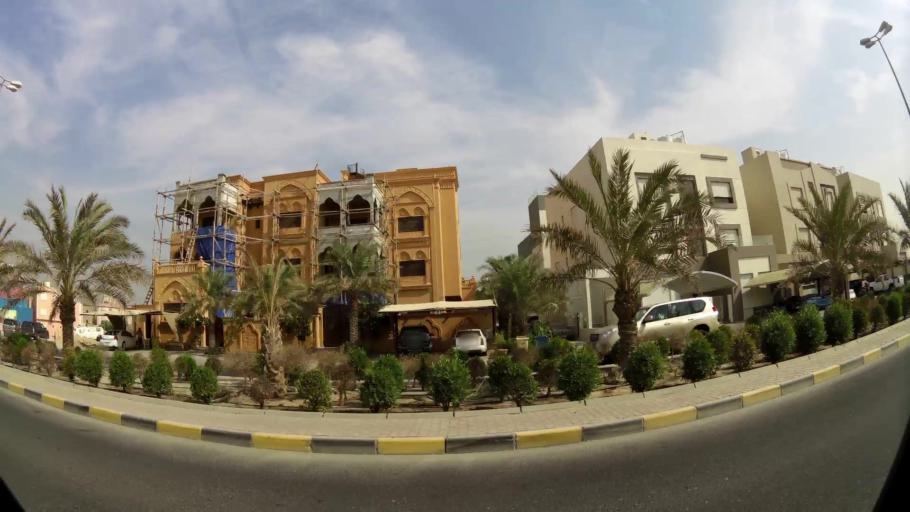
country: KW
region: Al Farwaniyah
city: Janub as Surrah
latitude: 29.2725
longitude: 47.9971
